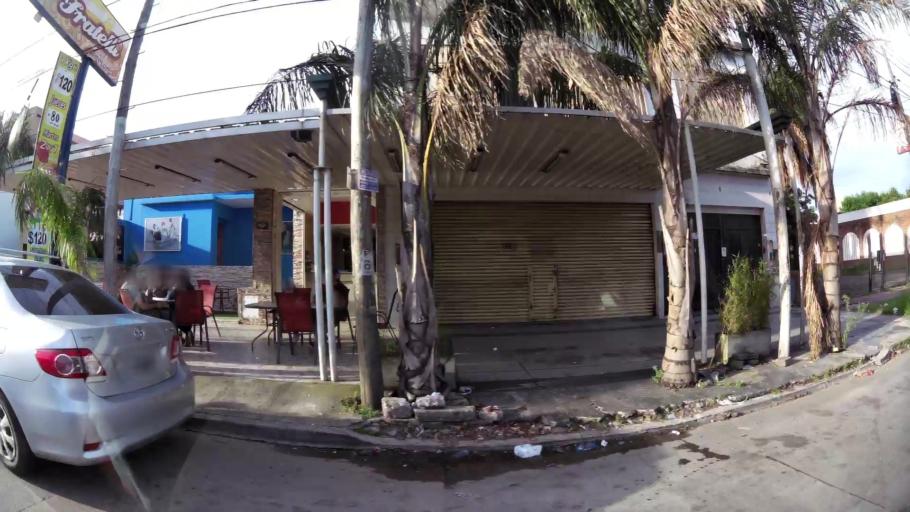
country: AR
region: Buenos Aires
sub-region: Partido de Moron
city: Moron
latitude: -34.6603
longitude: -58.6195
